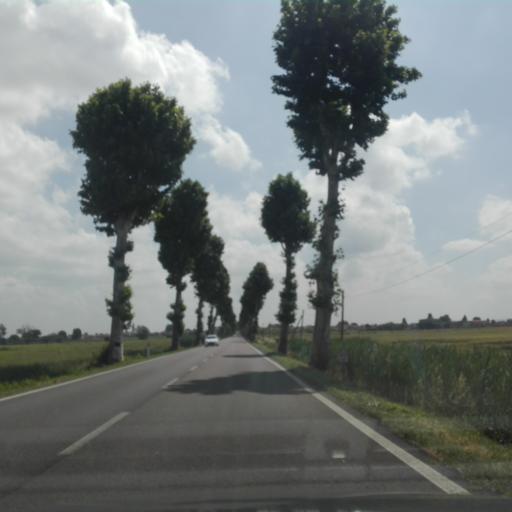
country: IT
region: Veneto
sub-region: Provincia di Rovigo
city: Buso
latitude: 45.0747
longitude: 11.8699
